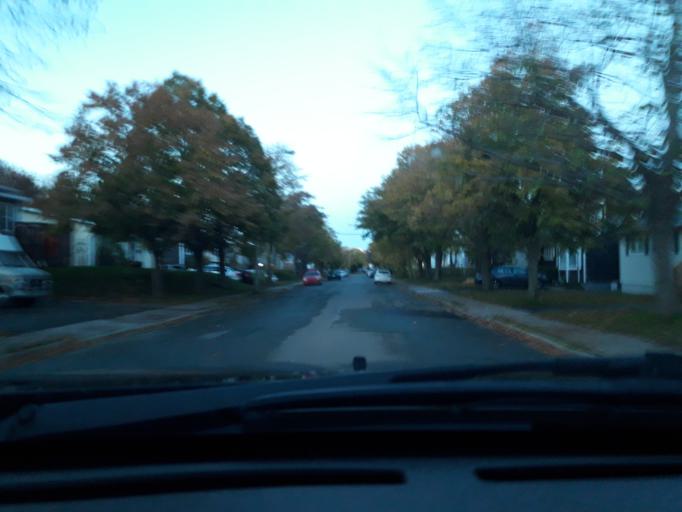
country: CA
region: Newfoundland and Labrador
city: St. John's
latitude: 47.5632
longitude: -52.7443
